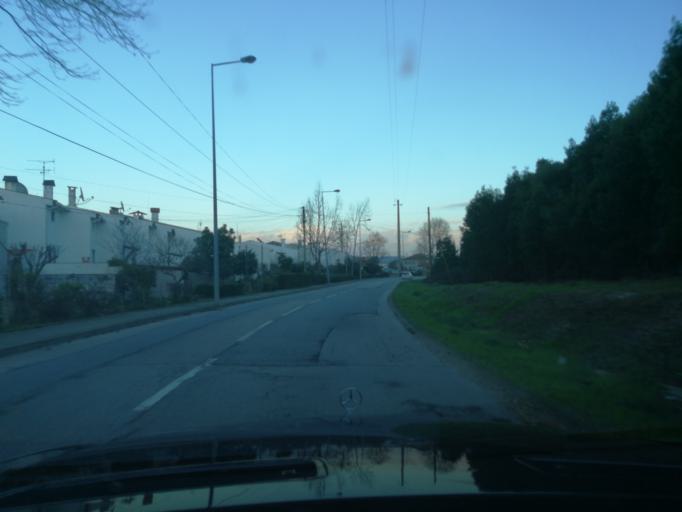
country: PT
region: Aveiro
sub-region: Estarreja
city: Estarreja
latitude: 40.7577
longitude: -8.5899
